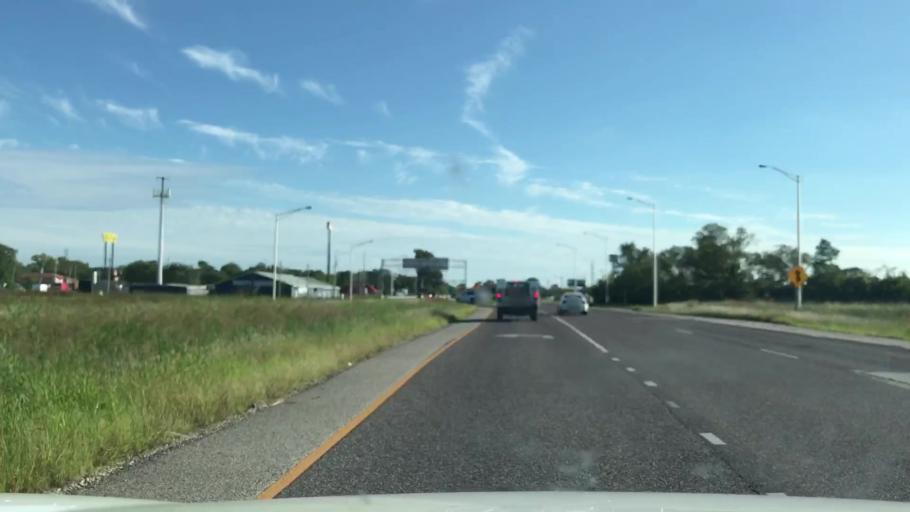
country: US
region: Illinois
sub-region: Madison County
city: Mitchell
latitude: 38.7652
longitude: -90.1243
